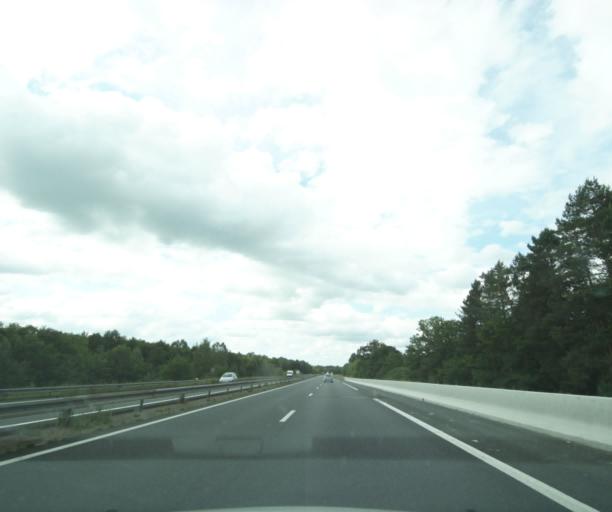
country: FR
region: Centre
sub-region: Departement du Loir-et-Cher
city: Nouan-le-Fuzelier
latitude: 47.5184
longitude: 2.0073
